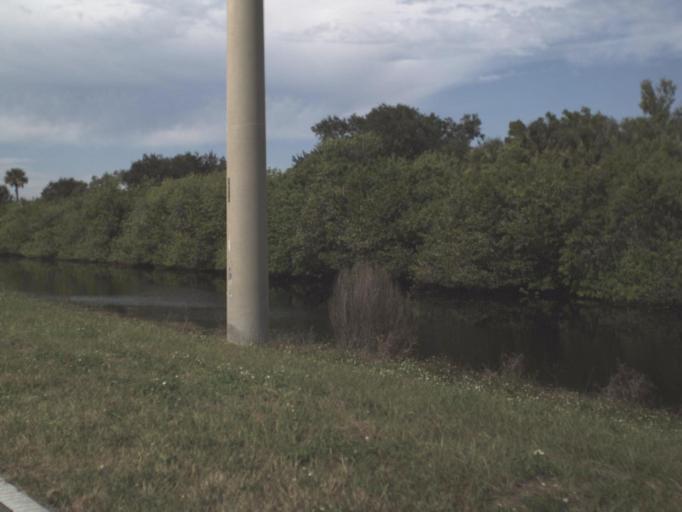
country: US
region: Florida
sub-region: Brevard County
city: Merritt Island
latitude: 28.5264
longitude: -80.7012
